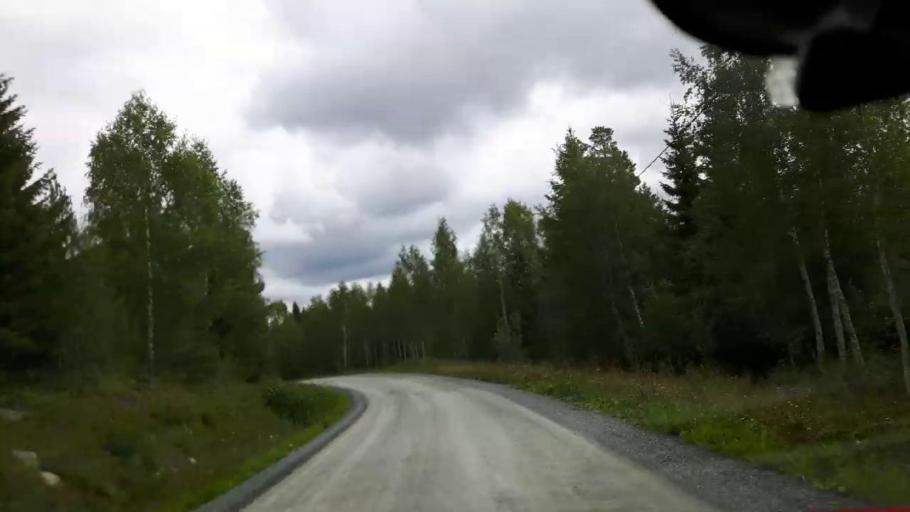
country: SE
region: Jaemtland
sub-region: Krokoms Kommun
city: Krokom
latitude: 63.5816
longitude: 14.1869
